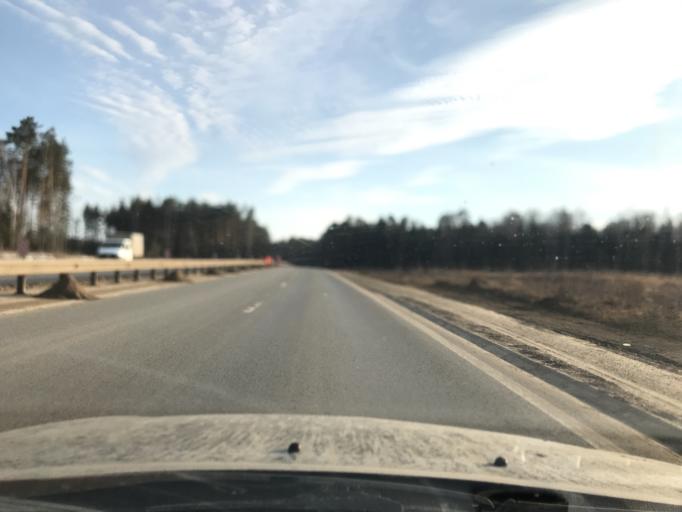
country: RU
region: Kaluga
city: Kaluga
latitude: 54.4174
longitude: 36.2009
